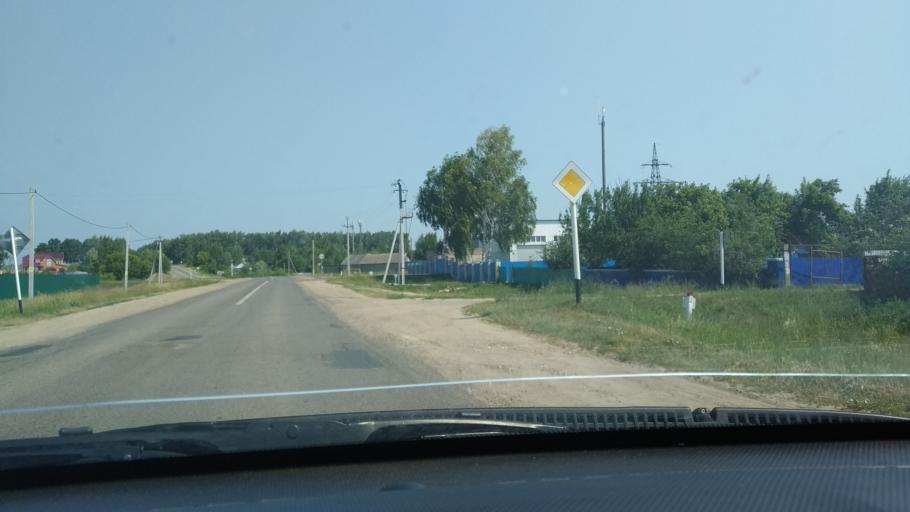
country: RU
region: Tatarstan
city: Osinovo
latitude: 55.9849
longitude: 48.8131
